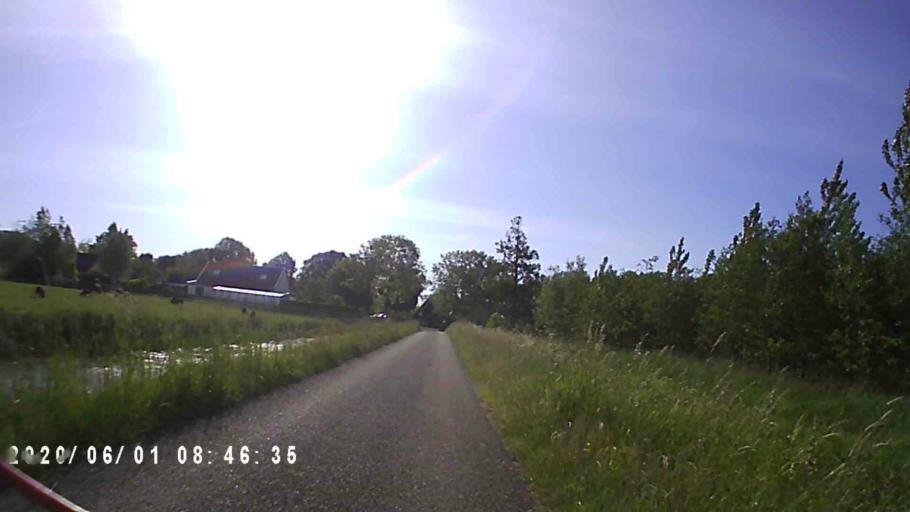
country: NL
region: Friesland
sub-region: Gemeente Ferwerderadiel
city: Burdaard
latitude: 53.2756
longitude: 5.8372
